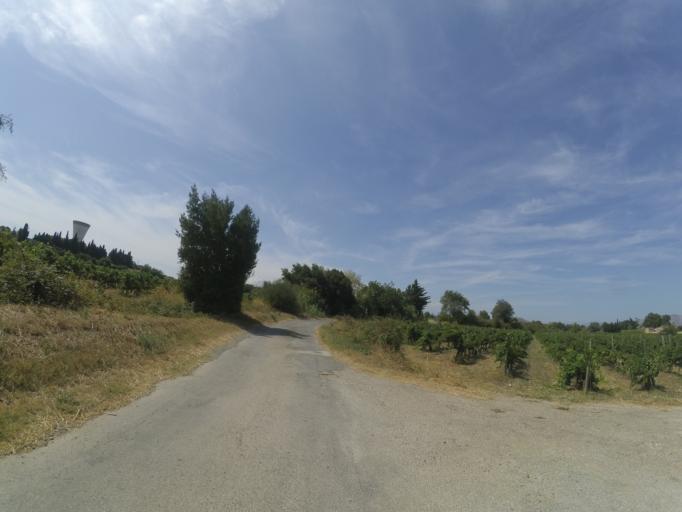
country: FR
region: Languedoc-Roussillon
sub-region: Departement des Pyrenees-Orientales
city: Rivesaltes
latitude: 42.7591
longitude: 2.8709
